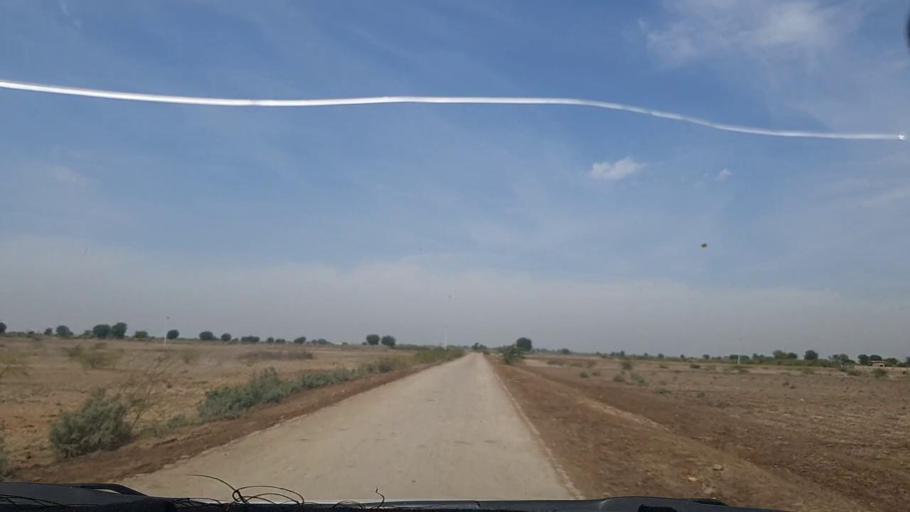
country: PK
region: Sindh
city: Pithoro
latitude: 25.4711
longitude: 69.4704
